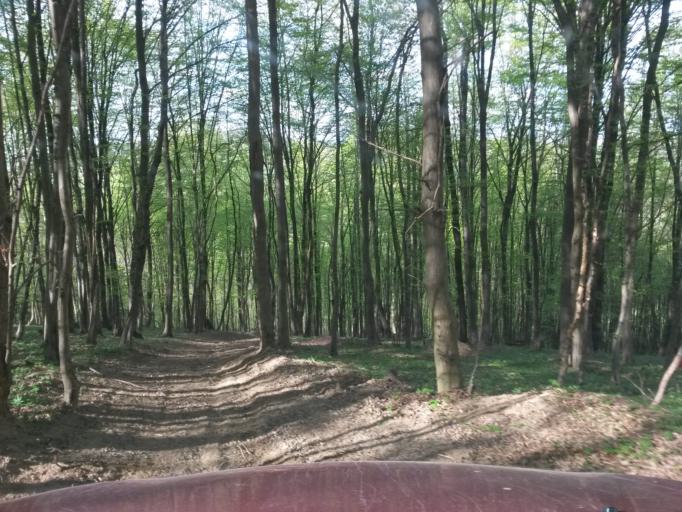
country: SK
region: Presovsky
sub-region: Okres Presov
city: Presov
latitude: 48.9523
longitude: 21.1501
